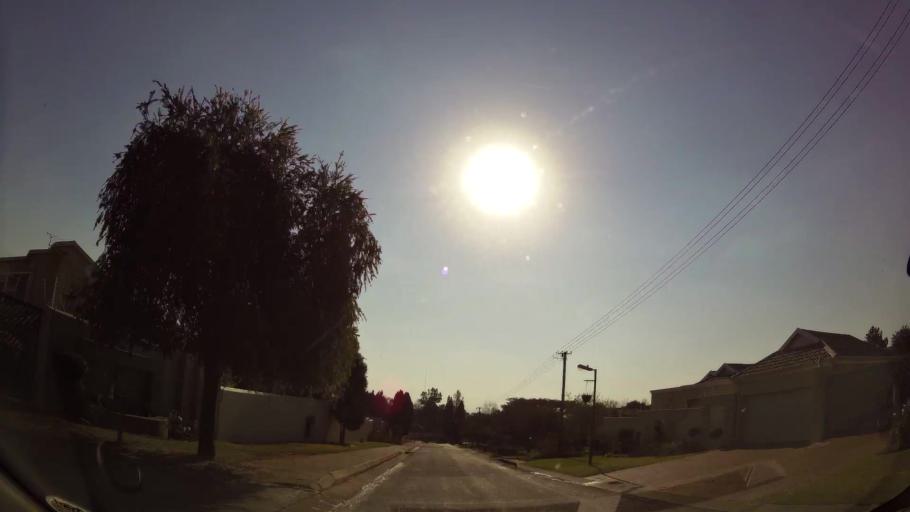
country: ZA
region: Gauteng
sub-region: City of Johannesburg Metropolitan Municipality
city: Diepsloot
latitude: -26.0694
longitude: 28.0122
